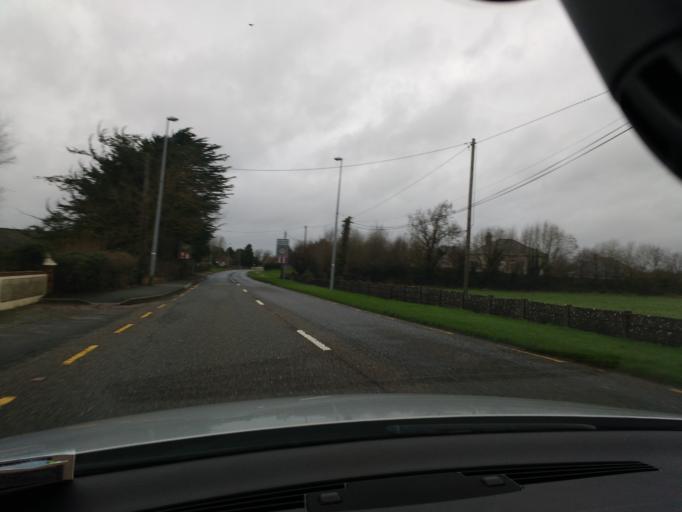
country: IE
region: Munster
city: Thurles
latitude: 52.6720
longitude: -7.7034
